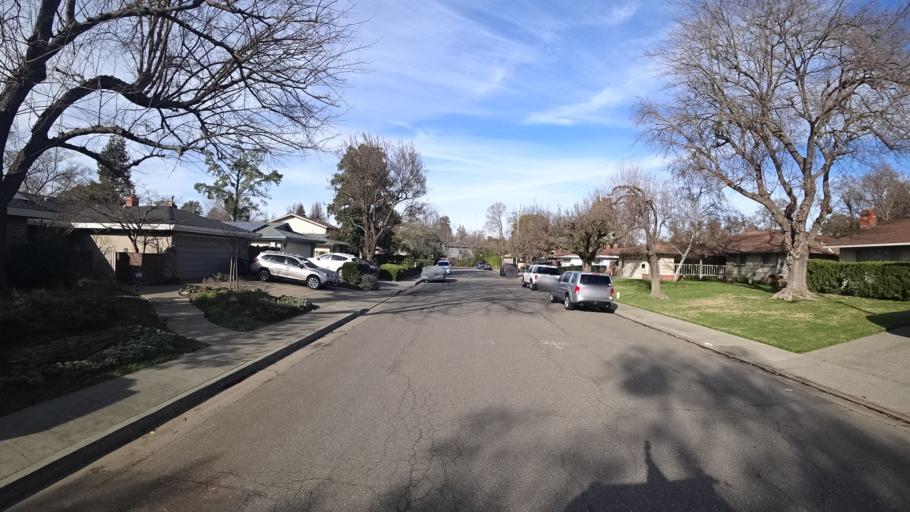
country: US
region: California
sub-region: Yolo County
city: Davis
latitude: 38.5473
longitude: -121.6951
